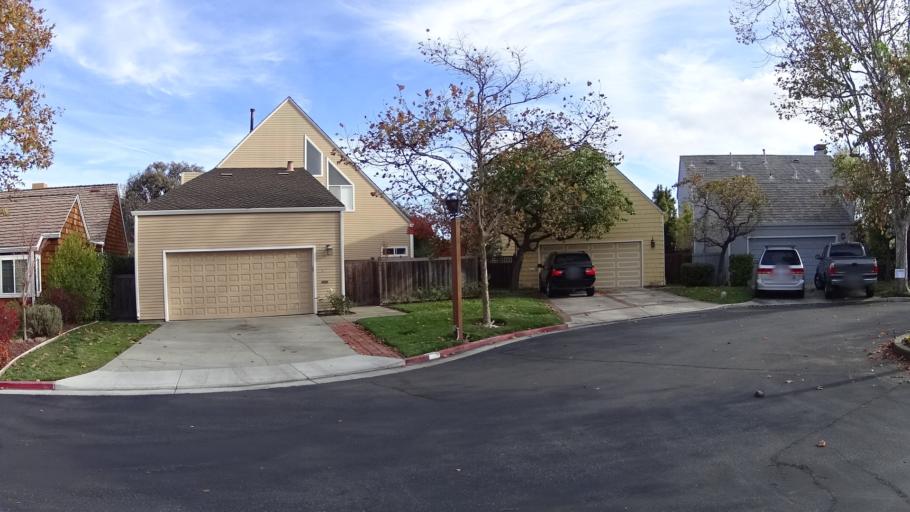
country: US
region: California
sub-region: San Mateo County
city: Foster City
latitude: 37.5422
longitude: -122.2665
